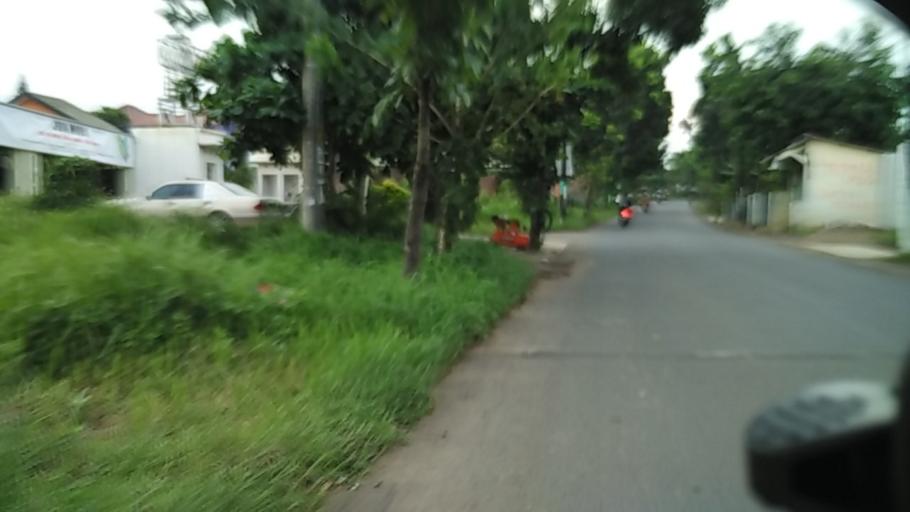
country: ID
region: Central Java
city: Semarang
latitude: -7.0683
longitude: 110.4333
